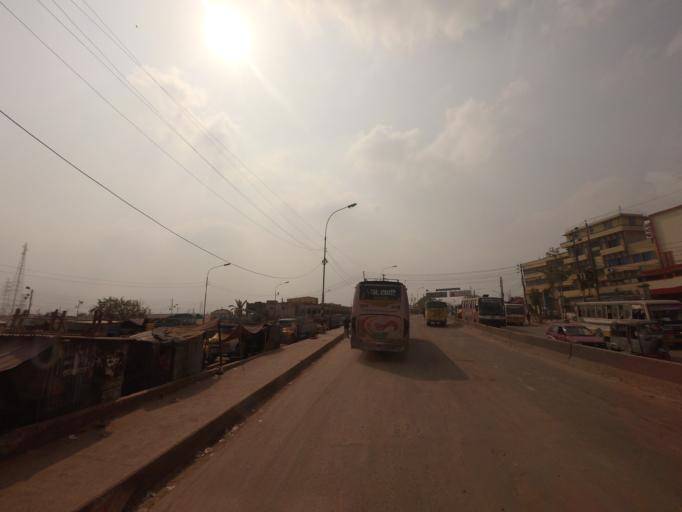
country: BD
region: Dhaka
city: Azimpur
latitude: 23.7831
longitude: 90.3387
